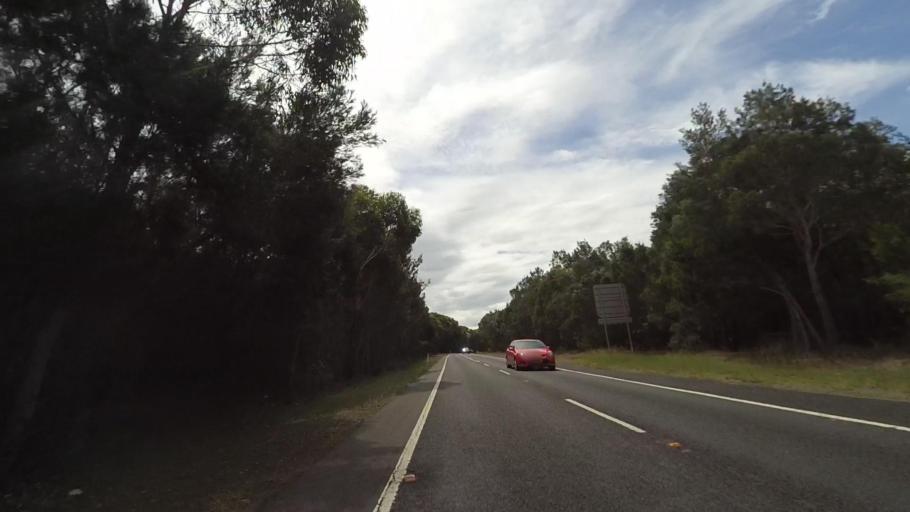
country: AU
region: New South Wales
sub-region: Sutherland Shire
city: Loftus
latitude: -34.0588
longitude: 151.0515
